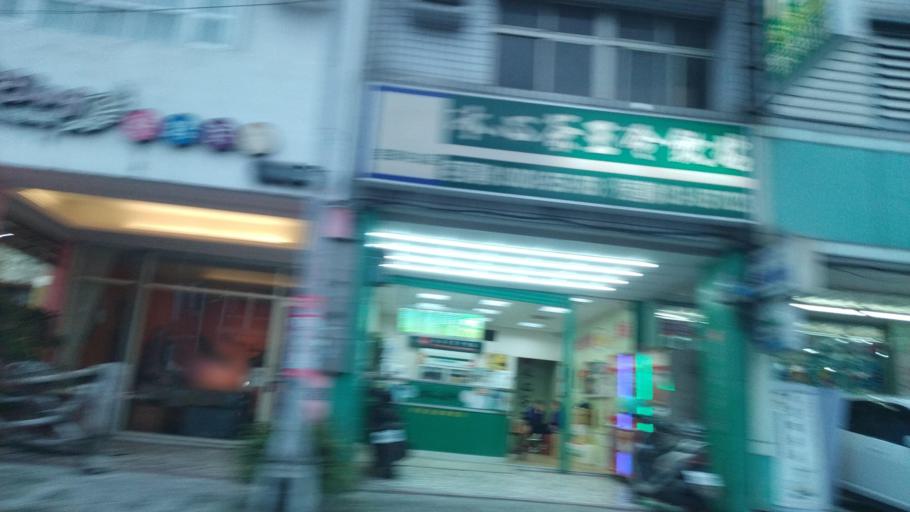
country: TW
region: Taiwan
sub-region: Hualien
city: Hualian
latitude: 23.9741
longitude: 121.5775
